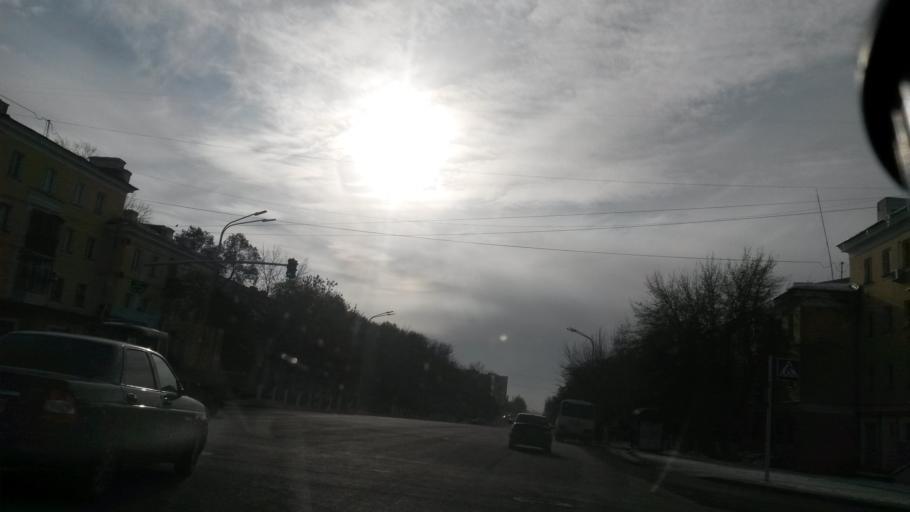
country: KZ
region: Qaraghandy
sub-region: Qaraghandy Qalasy
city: Karagandy
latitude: 49.8197
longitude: 73.0967
